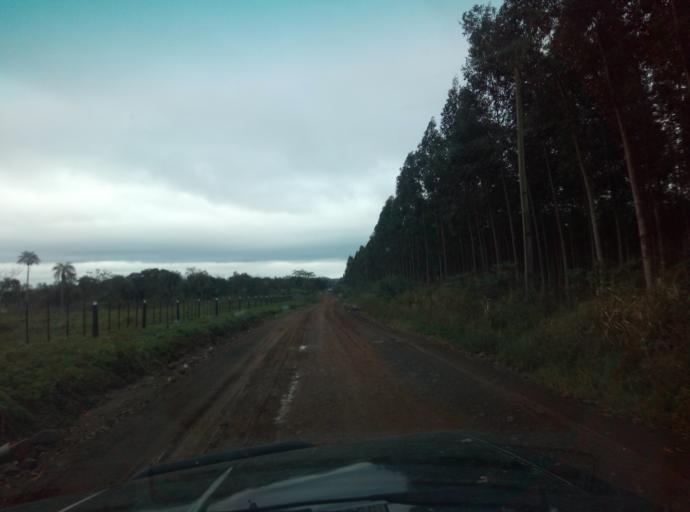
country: PY
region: Caaguazu
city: Carayao
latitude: -25.1902
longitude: -56.3852
